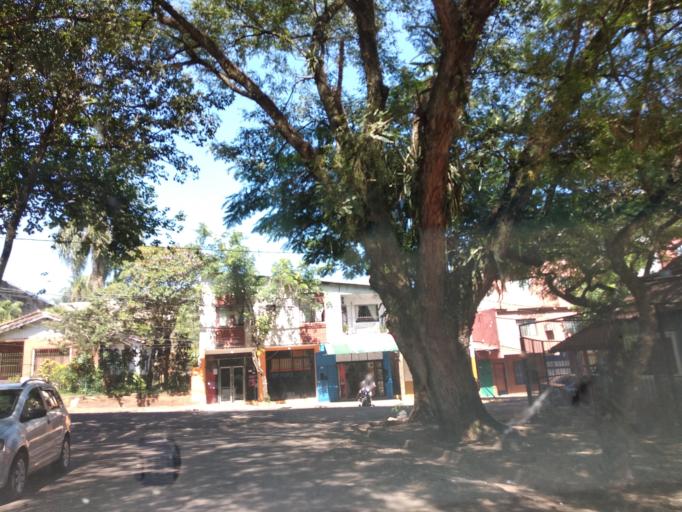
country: AR
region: Misiones
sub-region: Departamento de Iguazu
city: Puerto Iguazu
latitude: -25.5967
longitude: -54.5726
